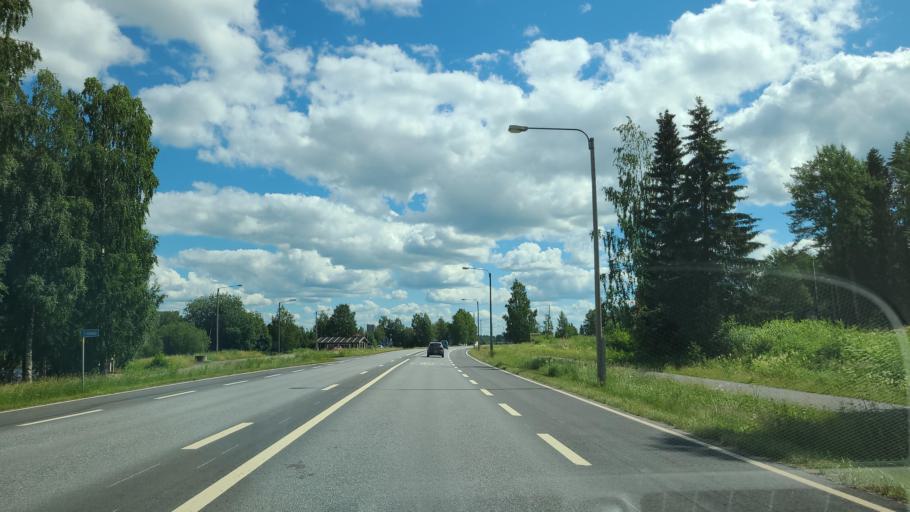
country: FI
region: Ostrobothnia
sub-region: Kyroenmaa
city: Isokyroe
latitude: 62.9740
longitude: 22.3764
